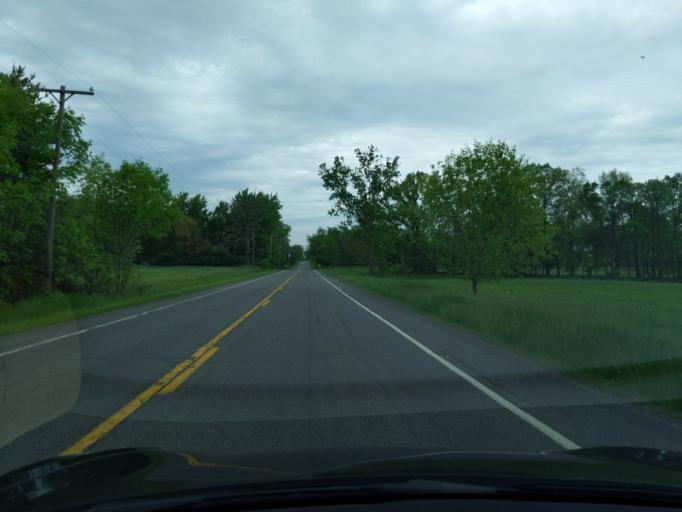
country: US
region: Michigan
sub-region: Ingham County
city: Mason
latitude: 42.5781
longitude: -84.3571
